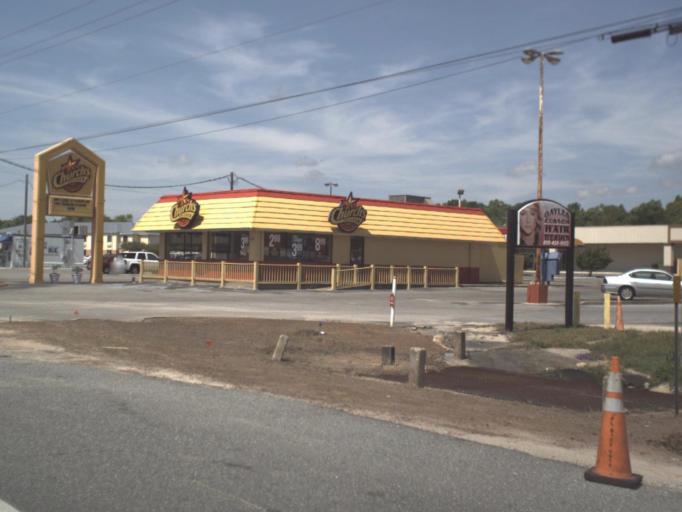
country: US
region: Florida
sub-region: Santa Rosa County
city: Milton
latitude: 30.6207
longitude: -87.0480
